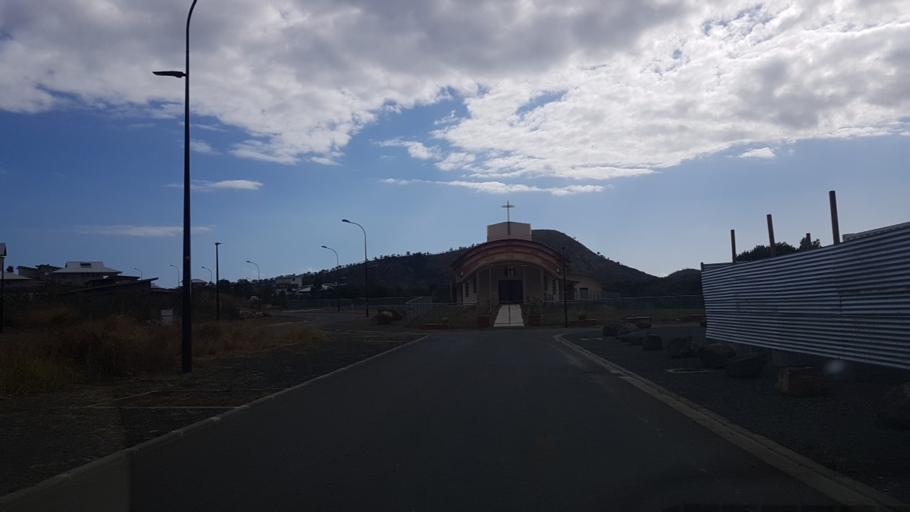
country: NC
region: South Province
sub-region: Dumbea
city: Dumbea
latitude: -22.1973
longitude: 166.4431
